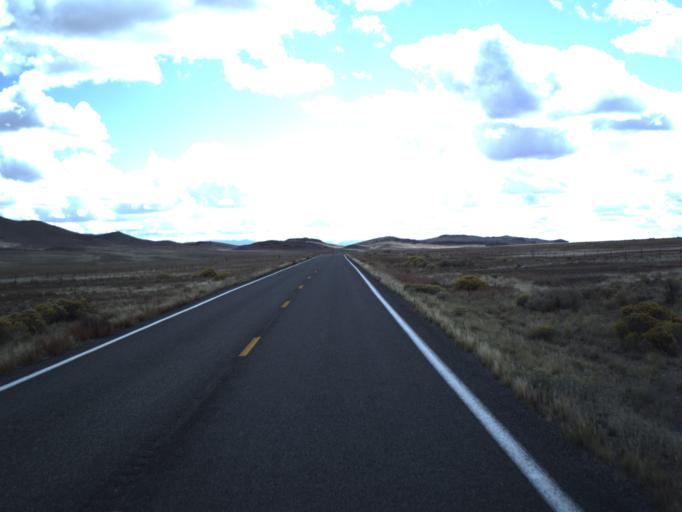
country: US
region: Utah
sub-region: Beaver County
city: Milford
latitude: 38.6574
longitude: -113.8745
